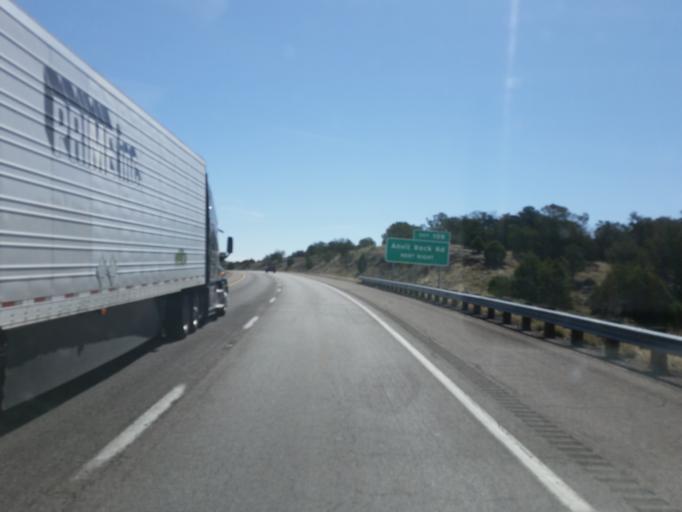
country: US
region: Arizona
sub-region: Mohave County
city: Peach Springs
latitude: 35.2856
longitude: -113.0964
